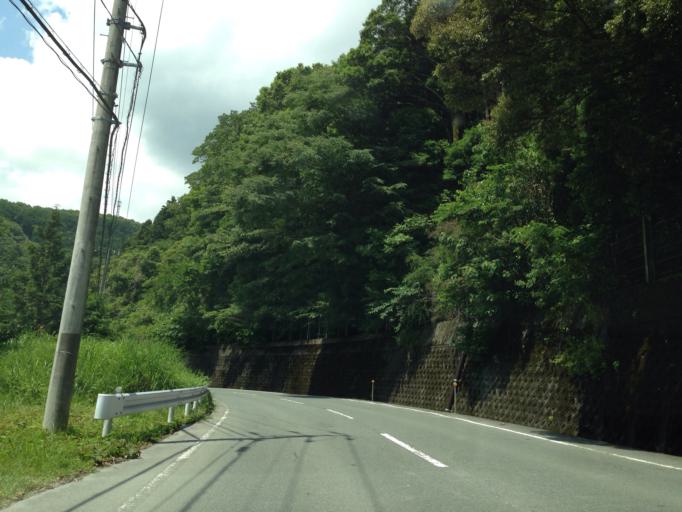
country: JP
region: Shizuoka
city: Heda
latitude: 34.9132
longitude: 138.8990
